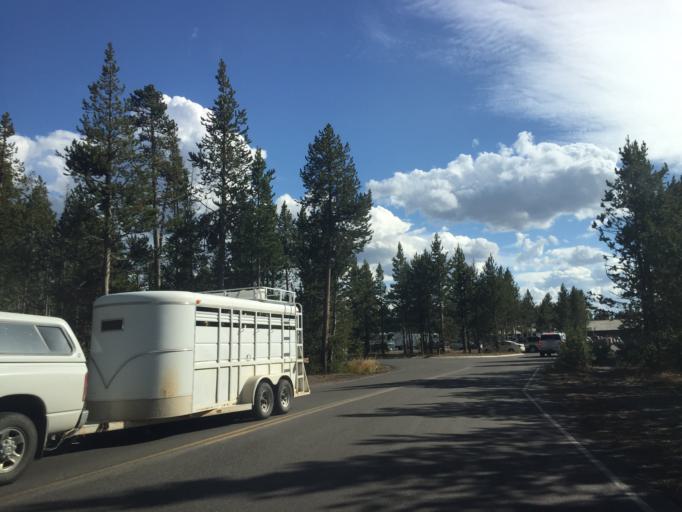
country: US
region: Montana
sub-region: Gallatin County
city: West Yellowstone
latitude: 44.7357
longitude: -110.4914
